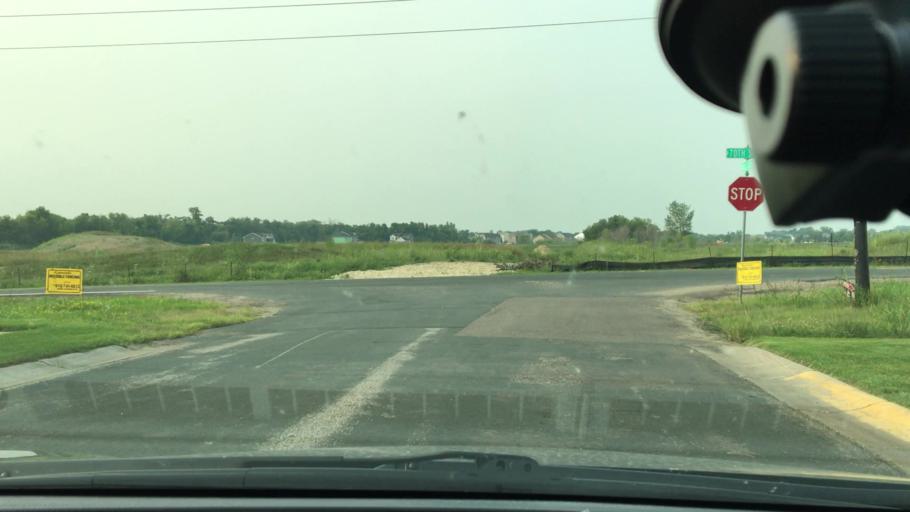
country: US
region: Minnesota
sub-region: Wright County
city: Albertville
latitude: 45.2523
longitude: -93.6455
